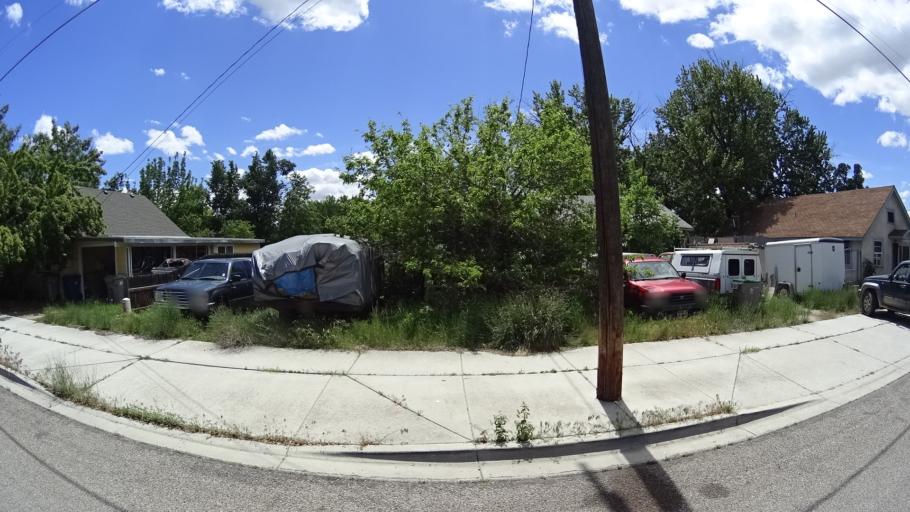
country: US
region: Idaho
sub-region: Ada County
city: Boise
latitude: 43.5946
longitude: -116.1862
